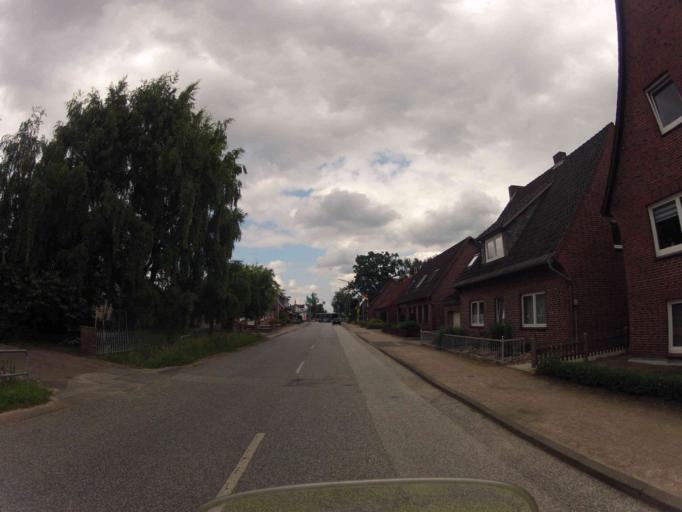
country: DE
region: Lower Saxony
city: Winsen
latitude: 53.4031
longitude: 10.1852
